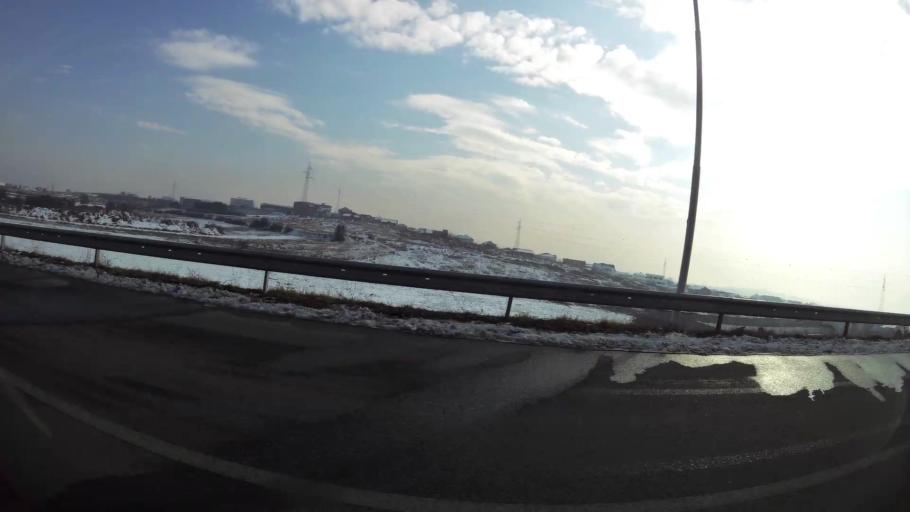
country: MK
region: Suto Orizari
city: Suto Orizare
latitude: 42.0514
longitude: 21.4220
